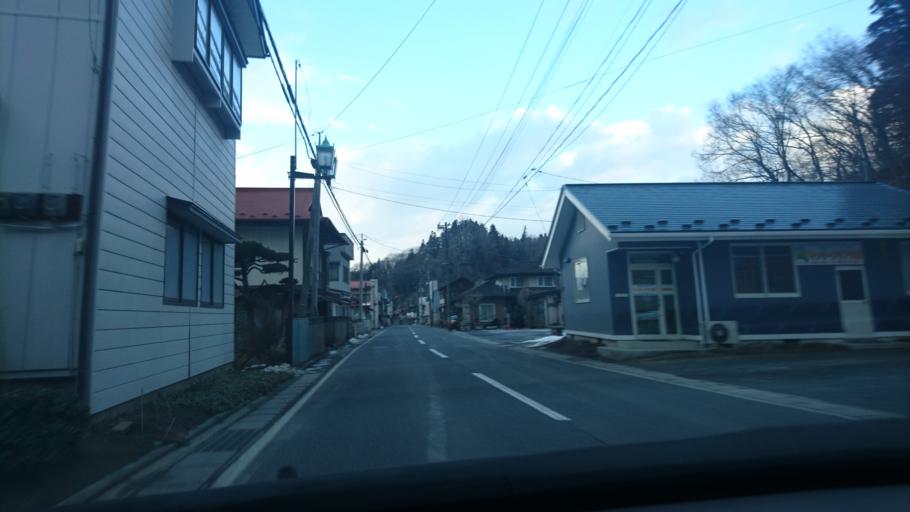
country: JP
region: Iwate
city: Ichinoseki
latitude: 38.9901
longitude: 141.3318
